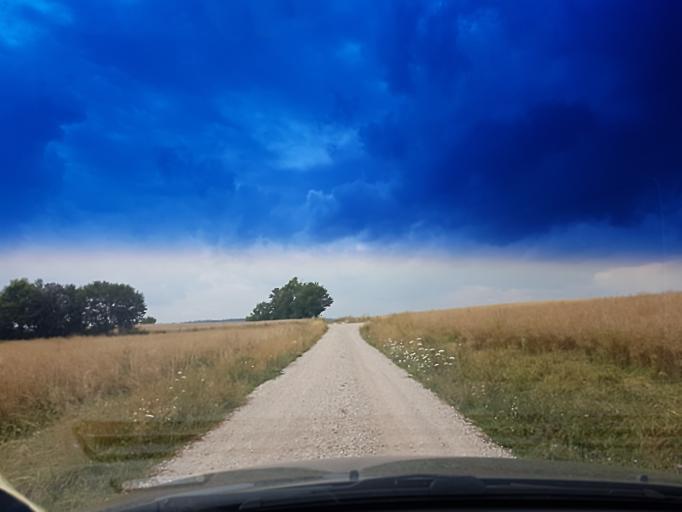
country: DE
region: Bavaria
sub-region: Upper Franconia
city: Rattelsdorf
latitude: 50.0571
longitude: 10.8850
